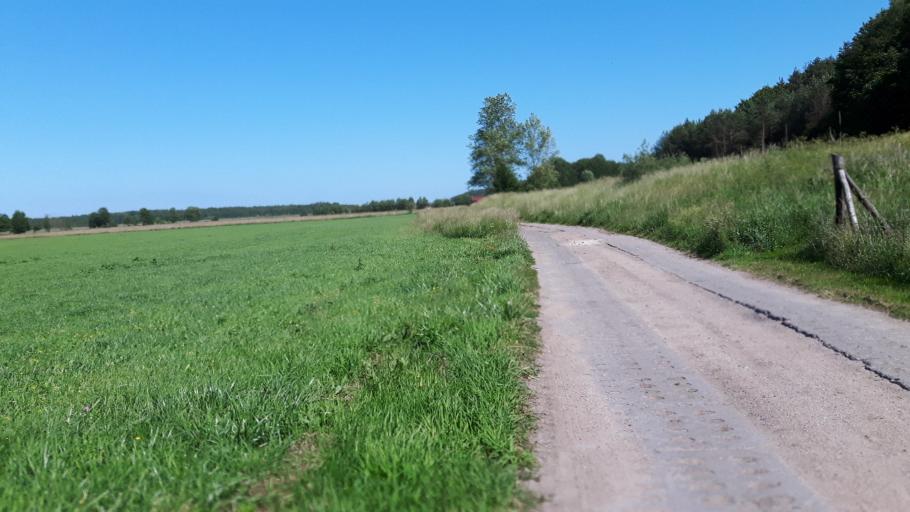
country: PL
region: Pomeranian Voivodeship
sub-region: Powiat slupski
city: Glowczyce
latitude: 54.6421
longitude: 17.3679
